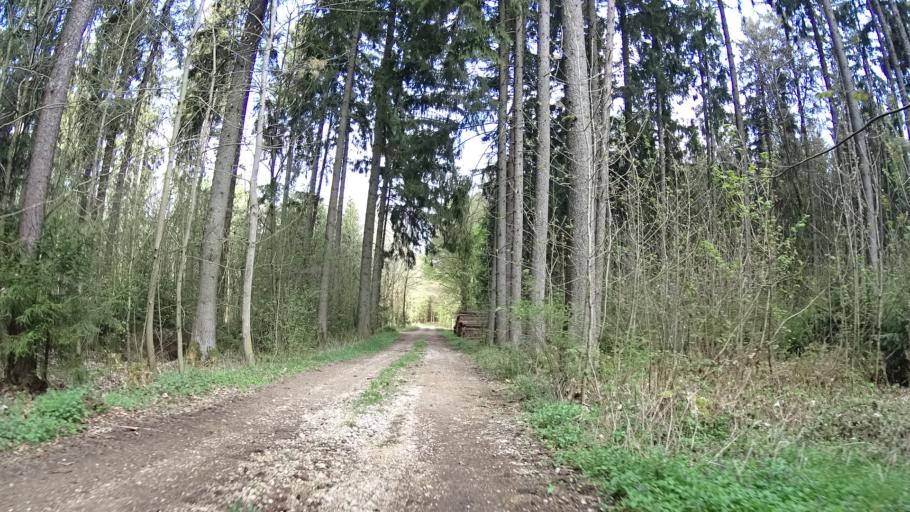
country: DE
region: Bavaria
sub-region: Upper Bavaria
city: Wettstetten
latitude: 48.8510
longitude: 11.4061
